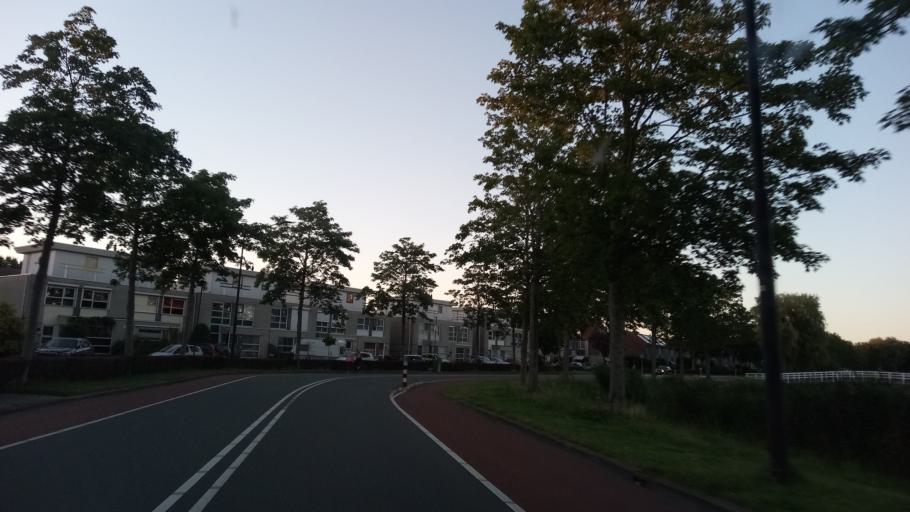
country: NL
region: North Holland
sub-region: Gemeente Langedijk
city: Broek op Langedijk
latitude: 52.6562
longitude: 4.8085
